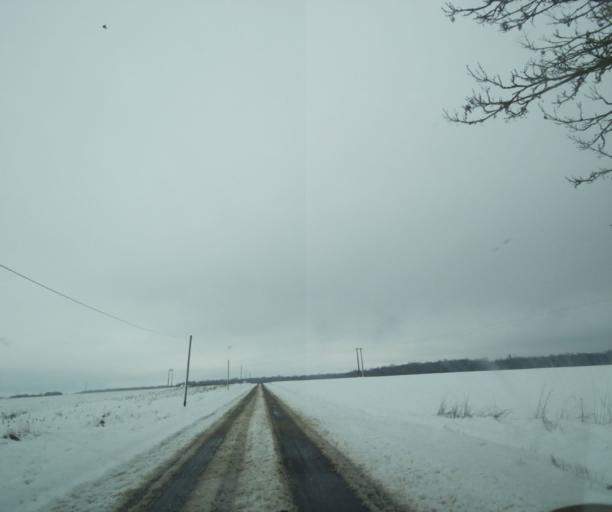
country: FR
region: Champagne-Ardenne
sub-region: Departement de la Haute-Marne
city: Montier-en-Der
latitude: 48.5122
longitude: 4.7716
